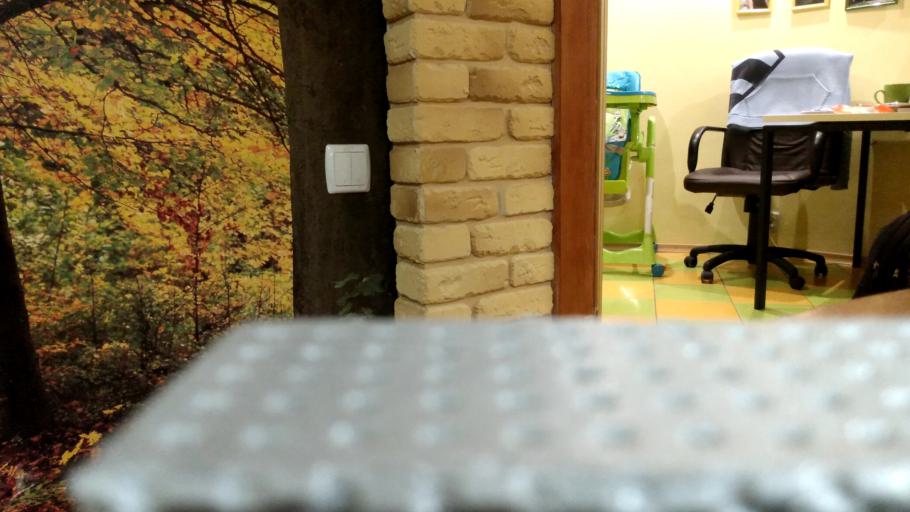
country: RU
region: Republic of Karelia
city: Pudozh
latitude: 61.8896
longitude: 37.6394
